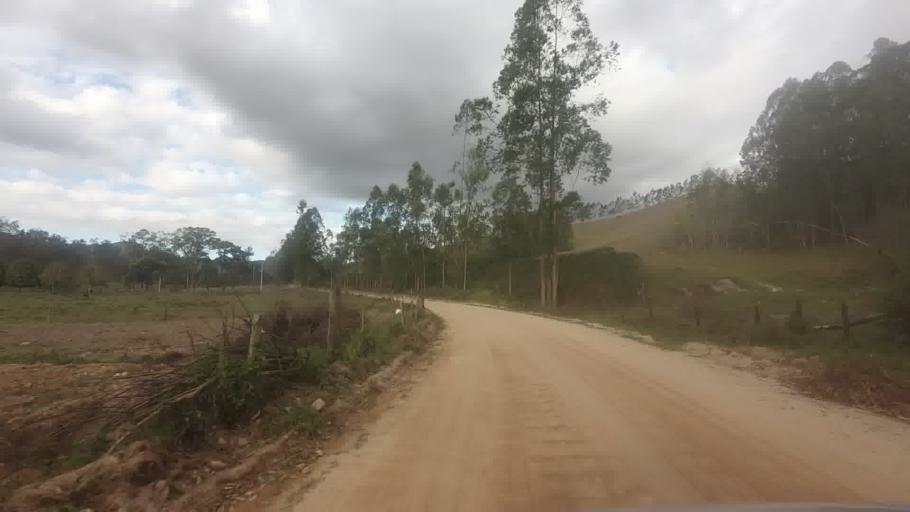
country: BR
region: Espirito Santo
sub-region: Mimoso Do Sul
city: Mimoso do Sul
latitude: -20.9540
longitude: -41.4273
